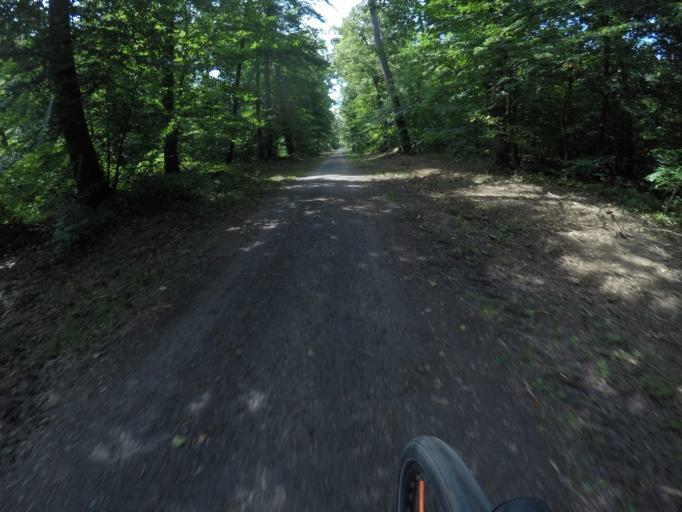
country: DE
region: Baden-Wuerttemberg
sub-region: Karlsruhe Region
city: Reilingen
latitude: 49.2771
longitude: 8.5681
